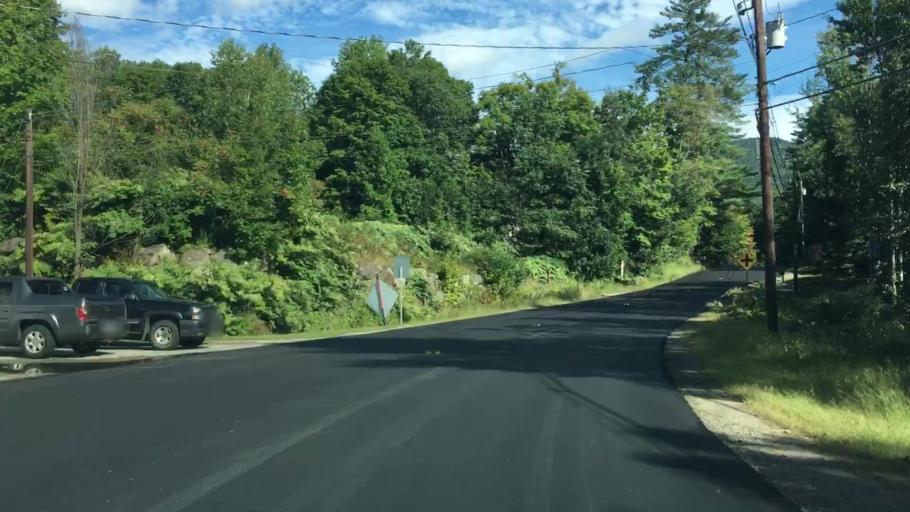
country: US
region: New Hampshire
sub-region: Grafton County
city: Woodstock
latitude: 44.0311
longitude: -71.6904
